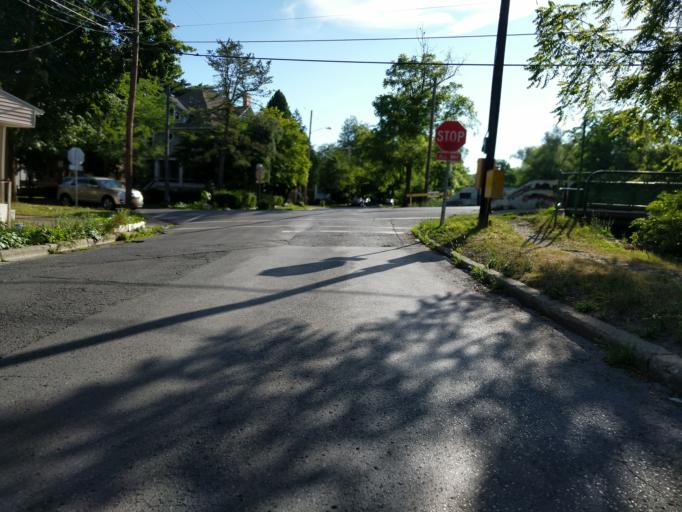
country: US
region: New York
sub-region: Tompkins County
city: Ithaca
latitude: 42.4343
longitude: -76.5010
